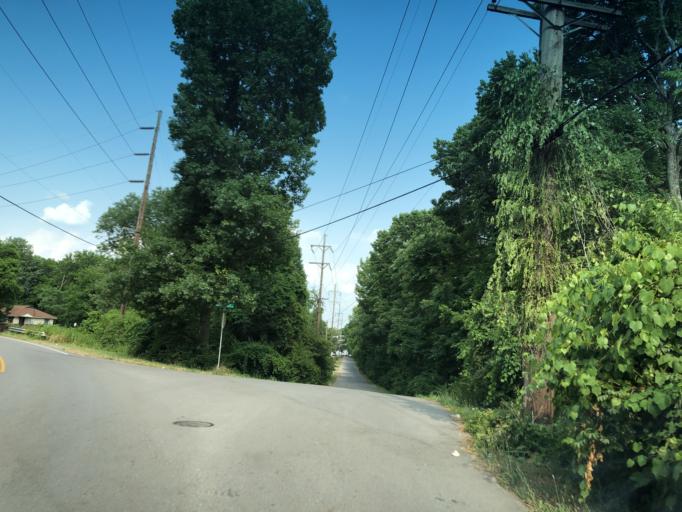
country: US
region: Tennessee
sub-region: Davidson County
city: Goodlettsville
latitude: 36.2749
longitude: -86.7163
